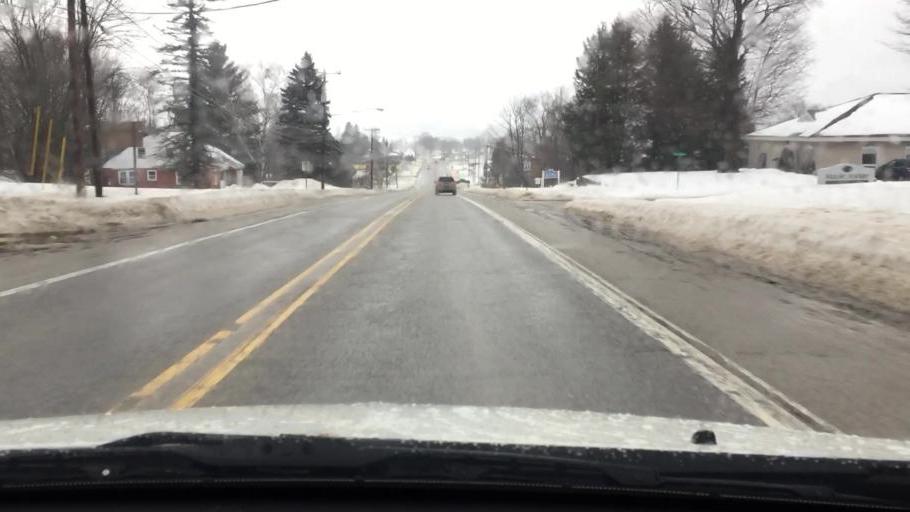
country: US
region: Michigan
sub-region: Charlevoix County
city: East Jordan
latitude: 45.1488
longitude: -85.1398
